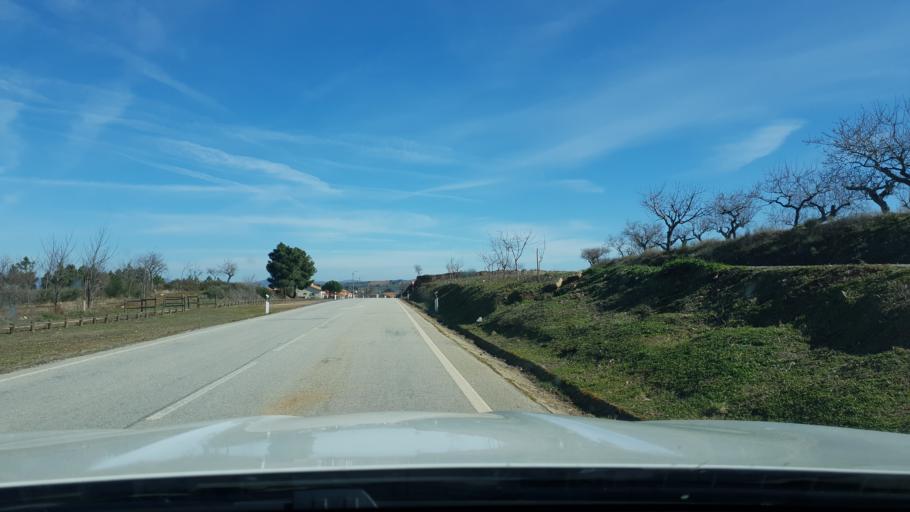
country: PT
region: Braganca
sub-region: Freixo de Espada A Cinta
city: Freixo de Espada a Cinta
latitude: 41.1813
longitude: -6.9056
